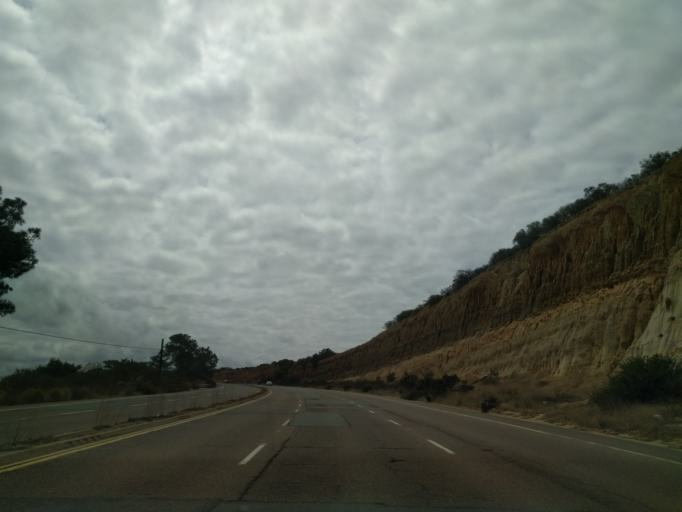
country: US
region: California
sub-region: San Diego County
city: Del Mar
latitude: 32.9190
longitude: -117.2489
